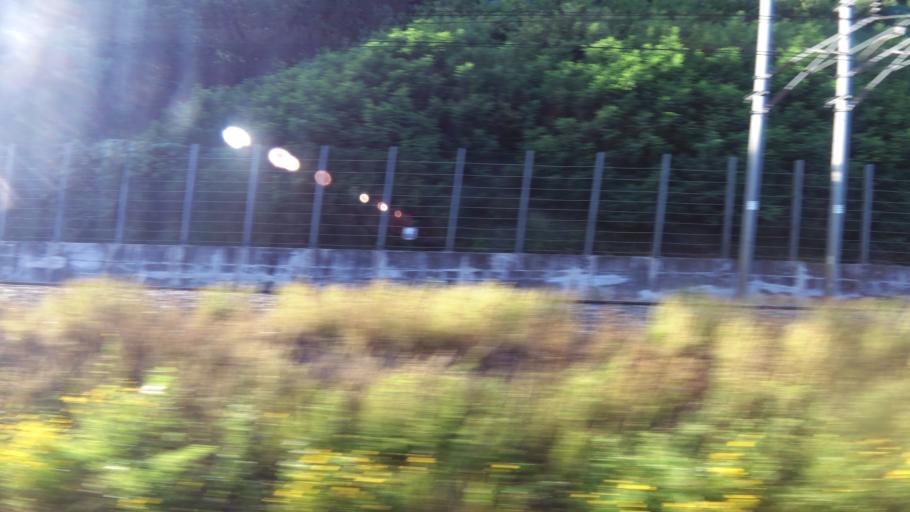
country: KR
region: Chungcheongbuk-do
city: Yong-dong
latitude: 36.1773
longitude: 127.8249
